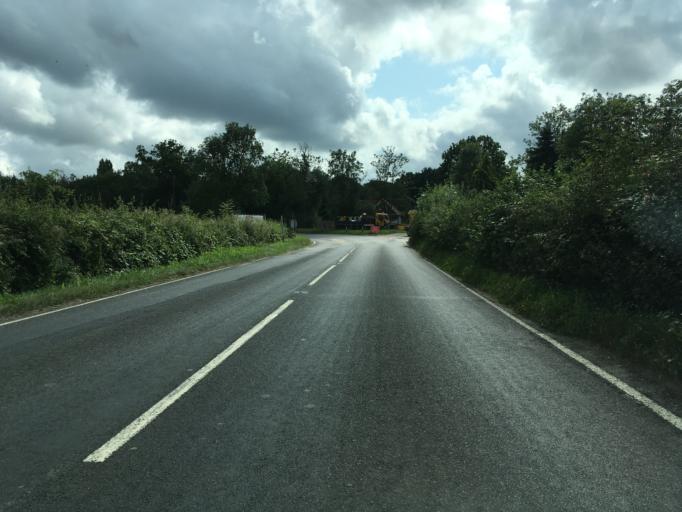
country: GB
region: England
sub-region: Kent
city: Tenterden
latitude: 51.1063
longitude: 0.6445
